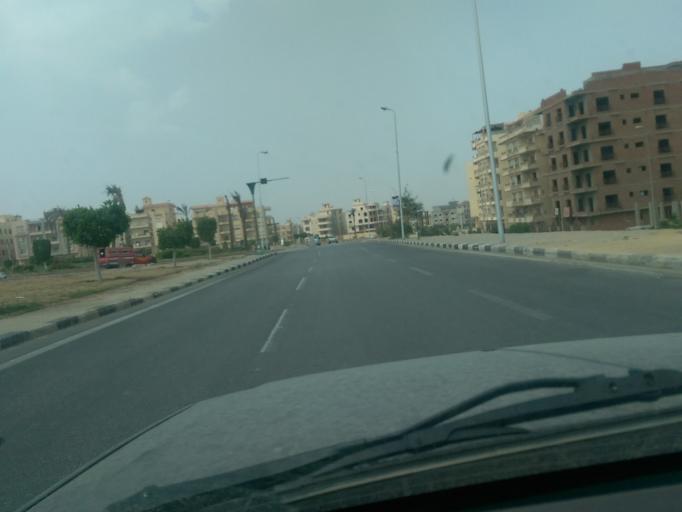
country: EG
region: Muhafazat al Qahirah
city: Cairo
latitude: 29.9919
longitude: 31.4318
